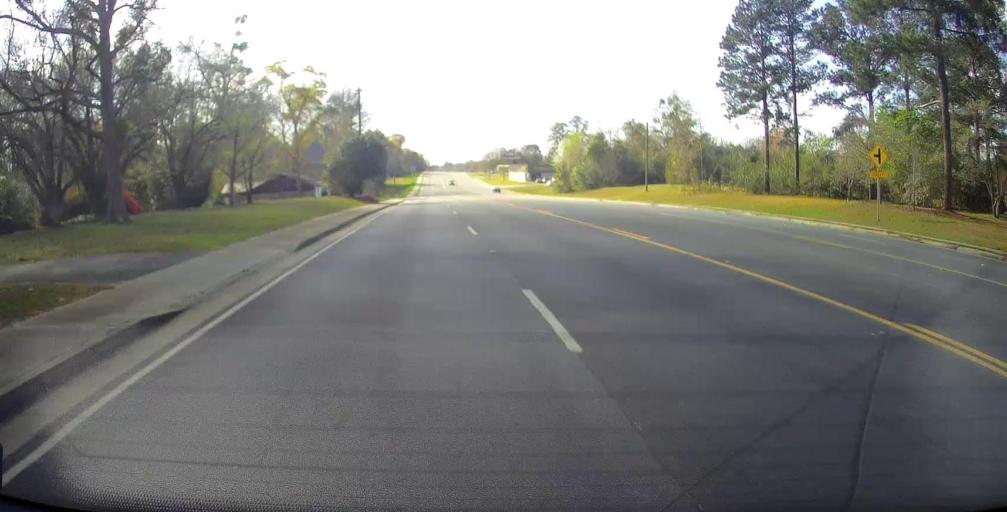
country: US
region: Georgia
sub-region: Dodge County
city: Eastman
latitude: 32.1050
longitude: -83.0672
